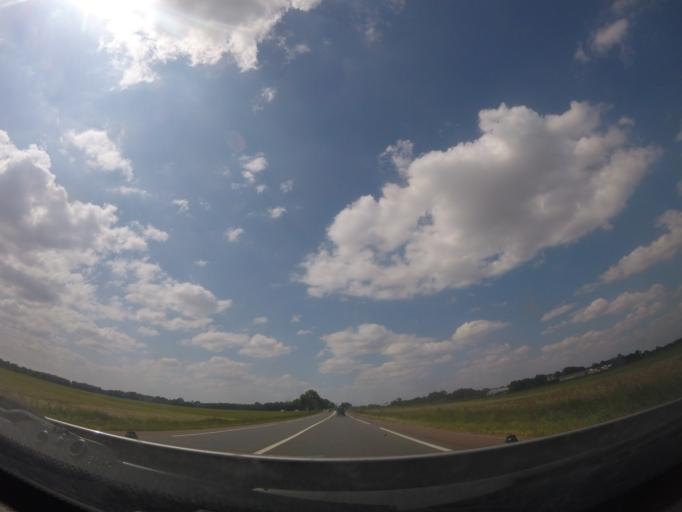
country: FR
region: Poitou-Charentes
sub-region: Departement de la Charente-Maritime
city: Saint-Porchaire
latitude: 45.8375
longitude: -0.8068
